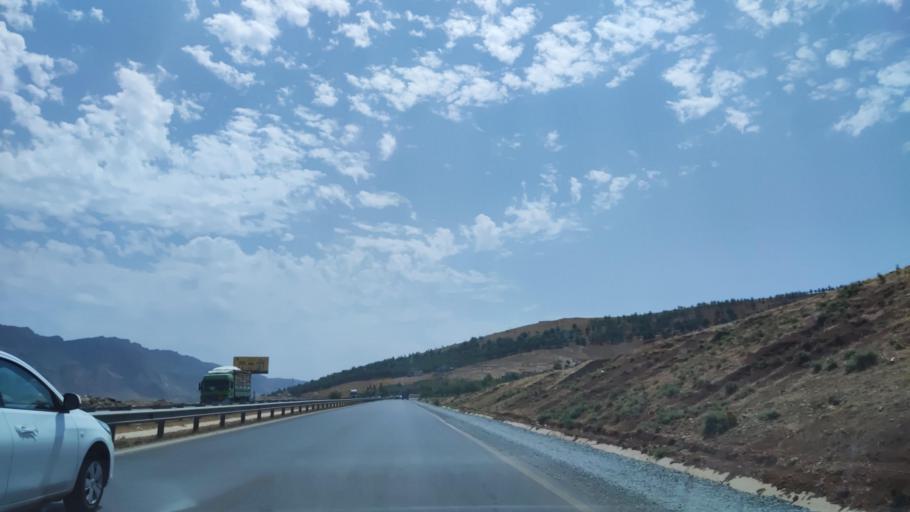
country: IQ
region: Arbil
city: Shaqlawah
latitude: 36.4955
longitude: 44.3660
